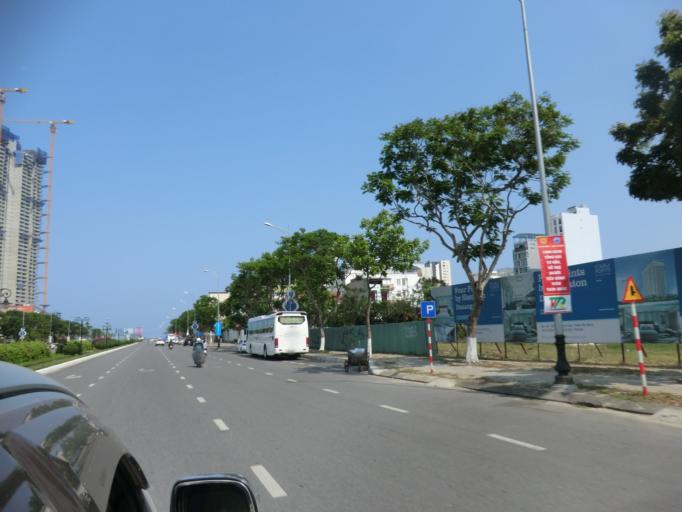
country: VN
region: Da Nang
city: Son Tra
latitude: 16.0700
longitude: 108.2402
